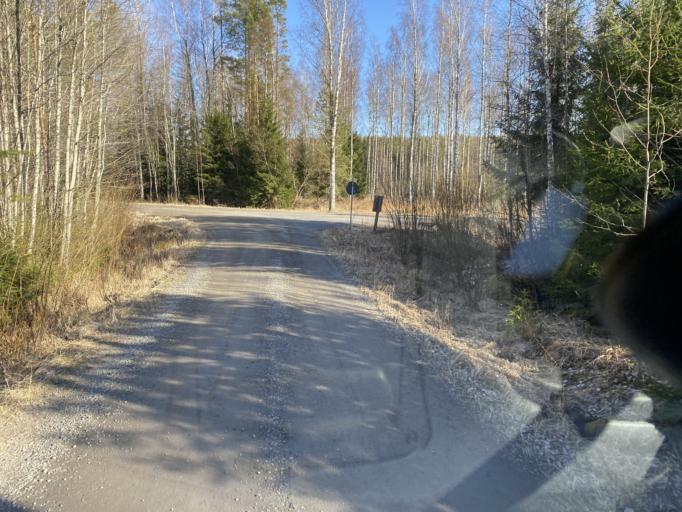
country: FI
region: Satakunta
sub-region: Rauma
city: Lappi
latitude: 61.1468
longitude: 21.9077
